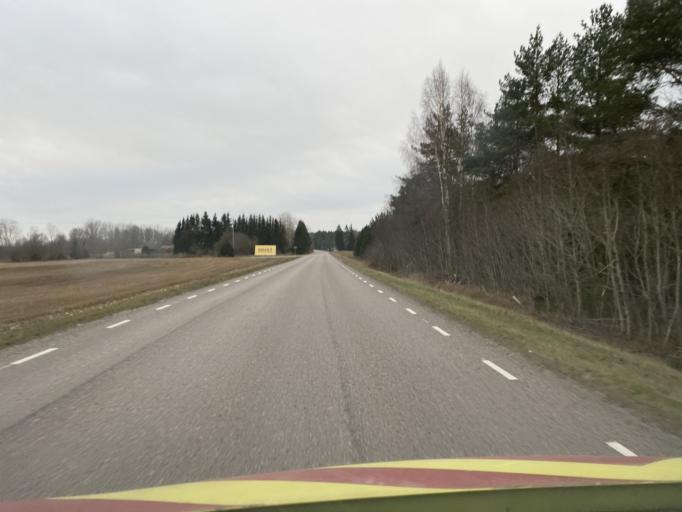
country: EE
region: Laeaene
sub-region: Ridala Parish
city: Uuemoisa
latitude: 59.0255
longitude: 23.6655
